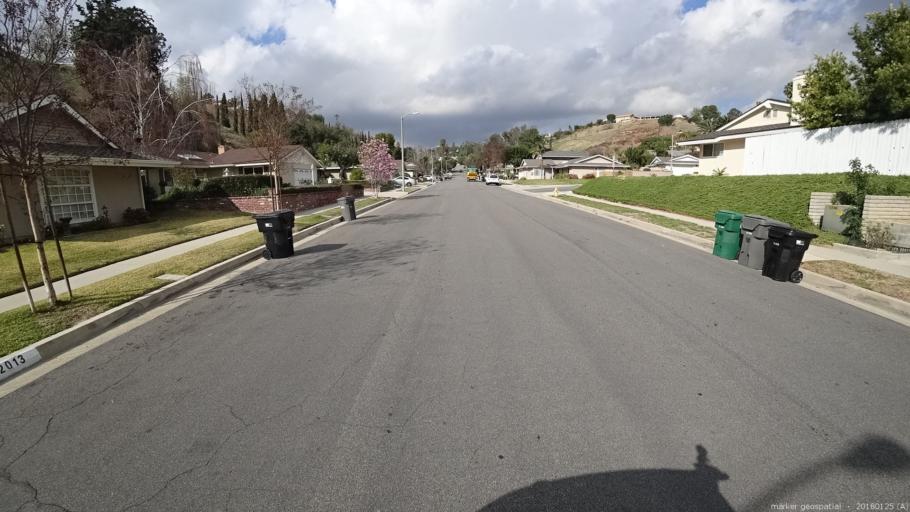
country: US
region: California
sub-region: Los Angeles County
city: Walnut
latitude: 33.9857
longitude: -117.8320
